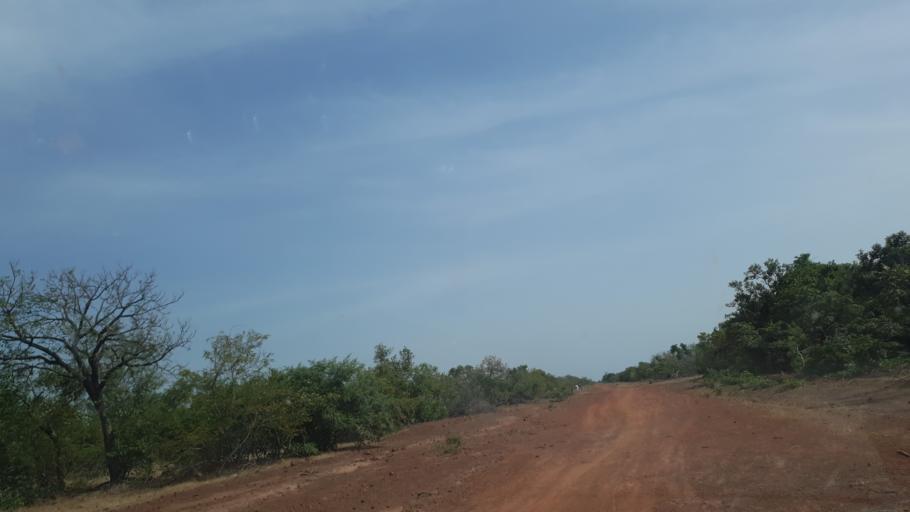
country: ML
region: Koulikoro
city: Dioila
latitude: 12.4379
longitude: -6.2106
